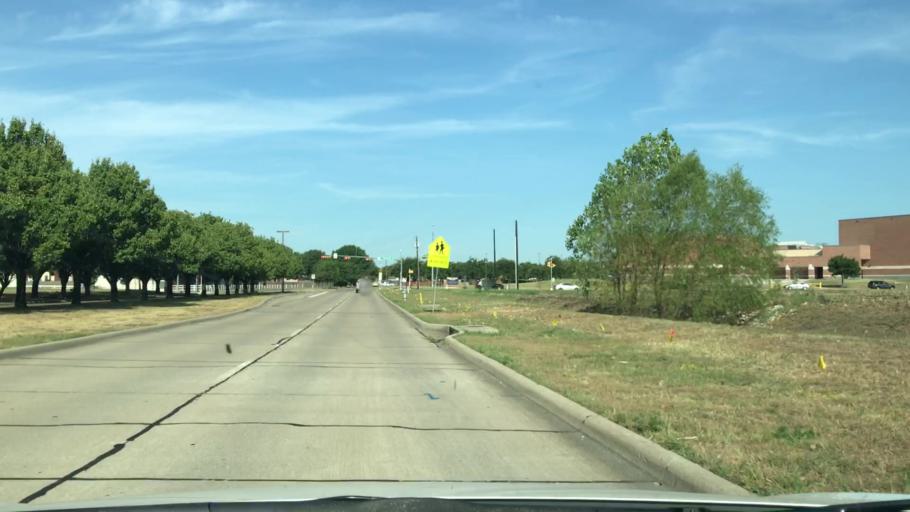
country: US
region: Texas
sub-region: Collin County
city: McKinney
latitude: 33.2294
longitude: -96.6389
